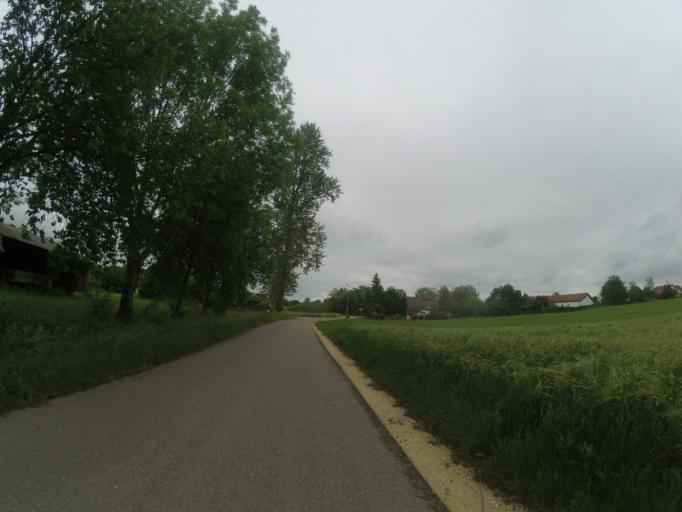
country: DE
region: Baden-Wuerttemberg
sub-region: Tuebingen Region
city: Langenau
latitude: 48.4980
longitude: 10.1027
